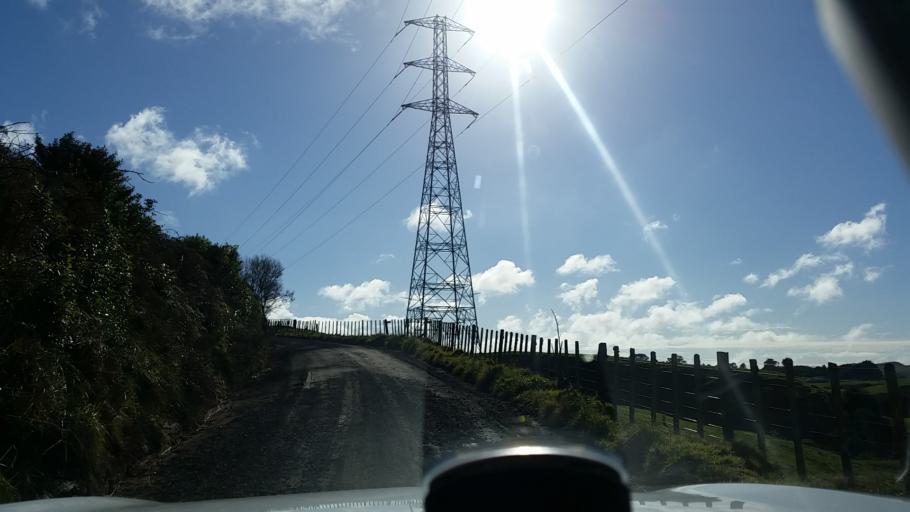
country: NZ
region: Taranaki
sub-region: South Taranaki District
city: Eltham
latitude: -39.4569
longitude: 174.3692
